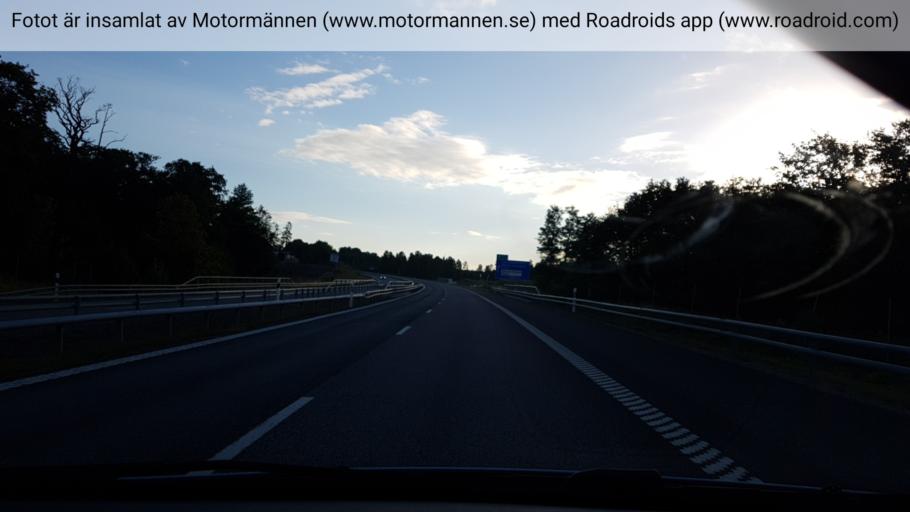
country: SE
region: Stockholm
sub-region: Haninge Kommun
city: Jordbro
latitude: 59.0994
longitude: 18.1151
